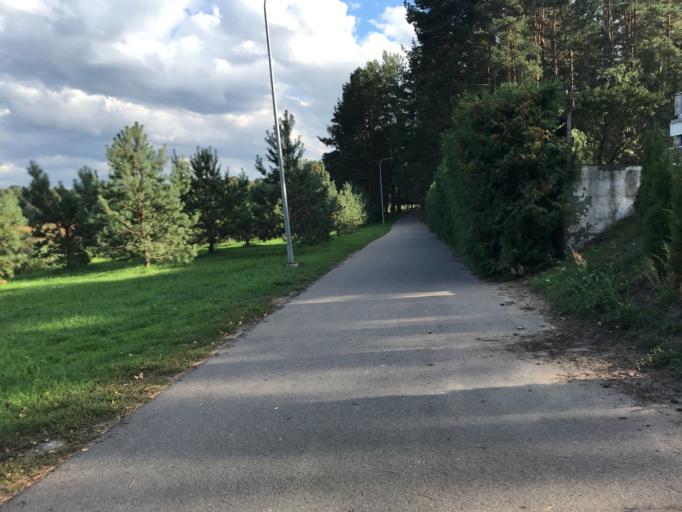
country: LT
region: Alytaus apskritis
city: Druskininkai
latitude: 54.0171
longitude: 23.9598
